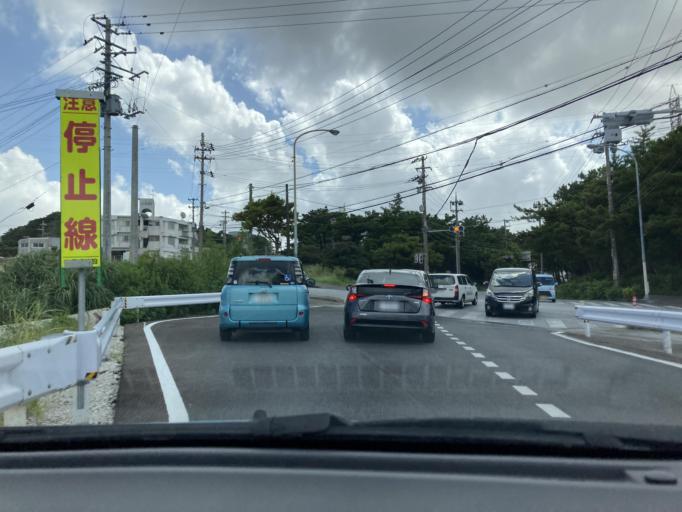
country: JP
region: Okinawa
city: Ginowan
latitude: 26.2576
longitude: 127.7245
